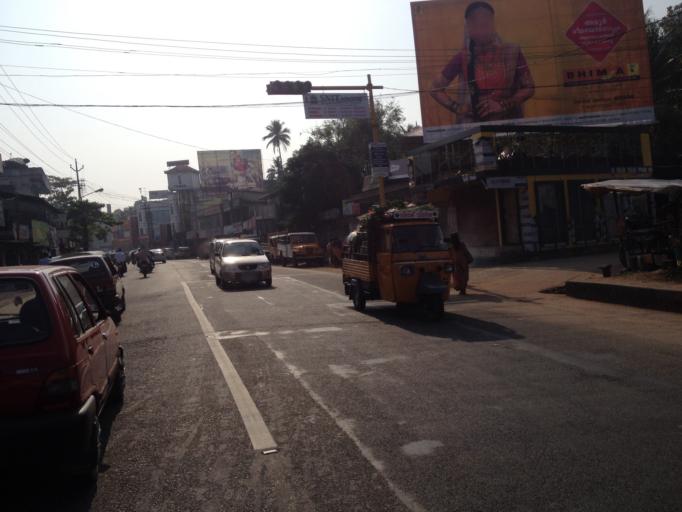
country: IN
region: Kerala
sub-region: Pattanamtitta
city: Adur
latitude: 9.1525
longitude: 76.7372
